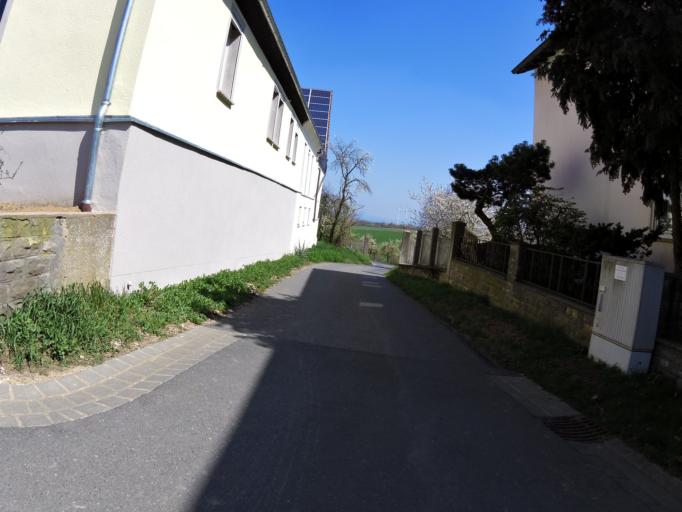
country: DE
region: Bavaria
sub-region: Regierungsbezirk Unterfranken
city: Biebelried
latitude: 49.7814
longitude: 10.0755
